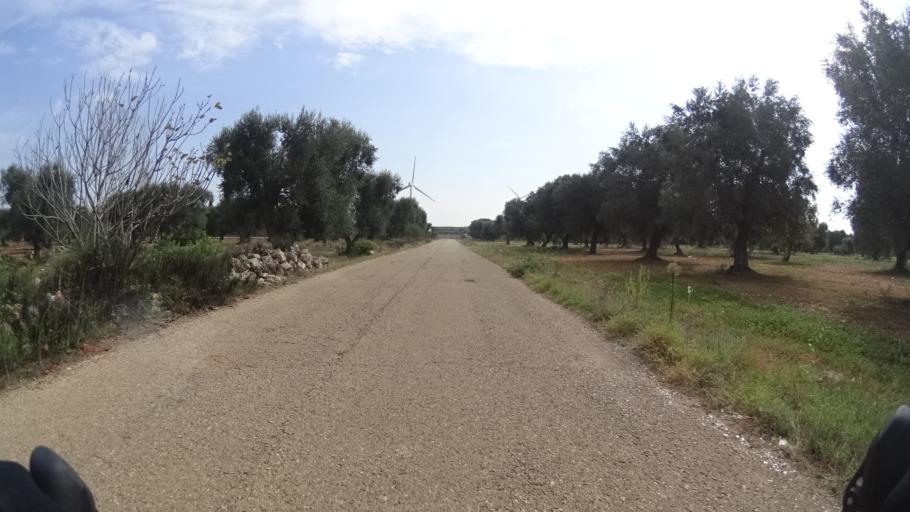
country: IT
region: Apulia
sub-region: Provincia di Taranto
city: San Marzano di San Giuseppe
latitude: 40.4382
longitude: 17.5364
